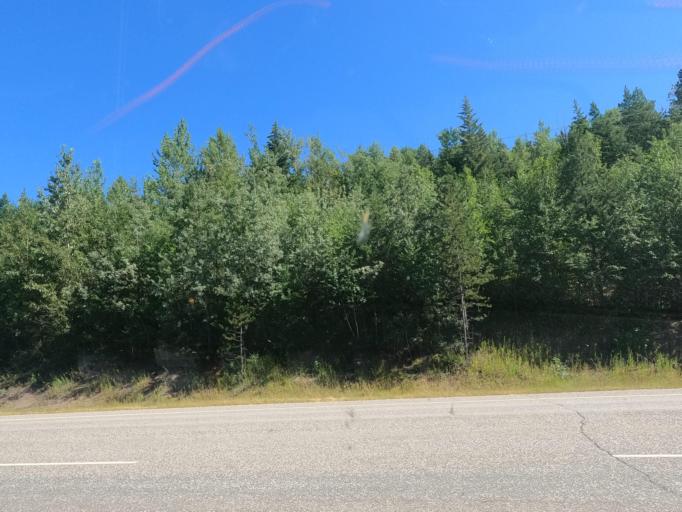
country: CA
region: British Columbia
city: Prince George
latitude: 53.4943
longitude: -122.6395
